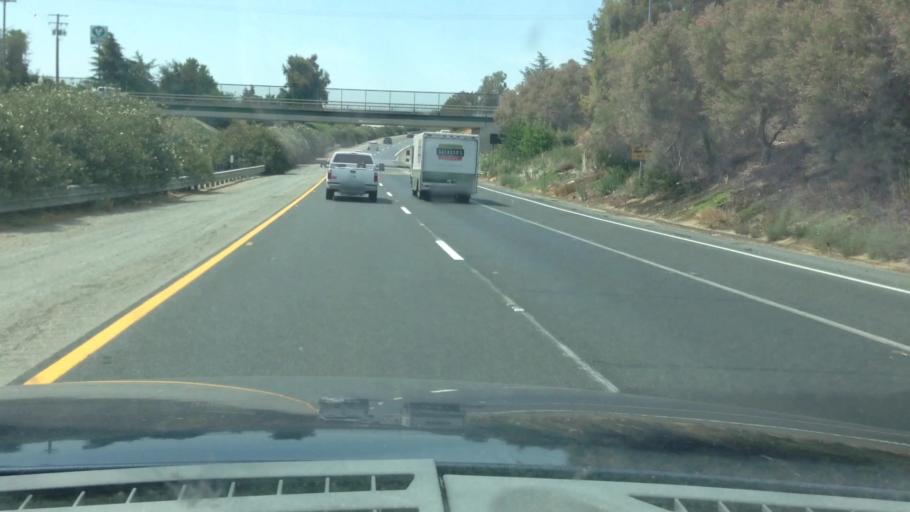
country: US
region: California
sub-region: Tulare County
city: Earlimart
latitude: 35.8785
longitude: -119.2709
